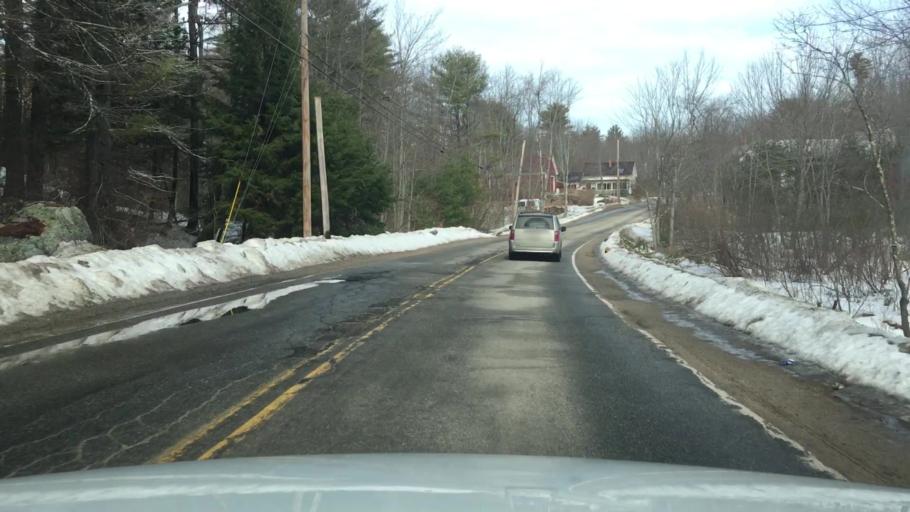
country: US
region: Maine
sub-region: York County
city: Springvale
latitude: 43.4866
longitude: -70.8076
